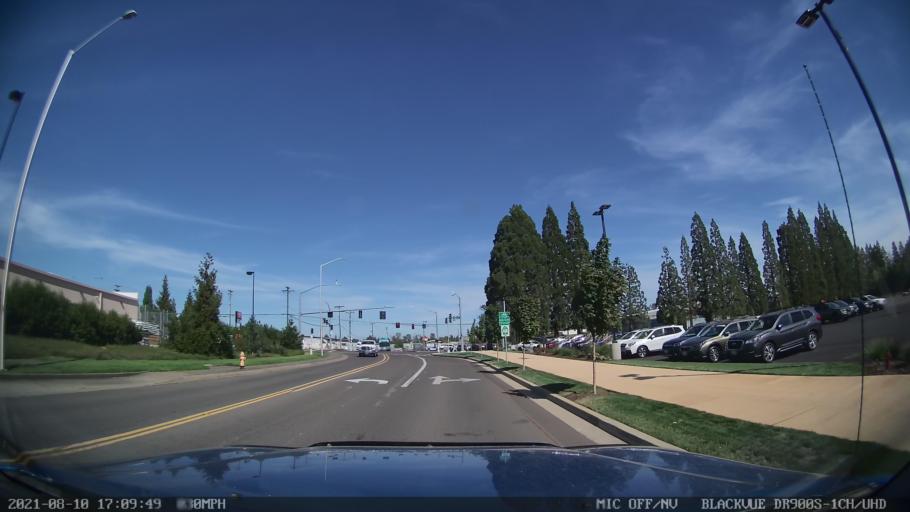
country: US
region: Oregon
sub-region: Marion County
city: Keizer
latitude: 44.9694
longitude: -123.0211
